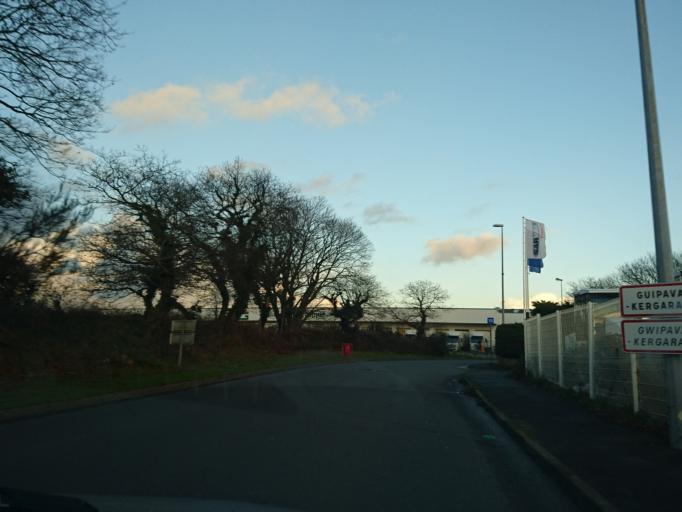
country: FR
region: Brittany
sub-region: Departement du Finistere
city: Gouesnou
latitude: 48.4318
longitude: -4.4454
